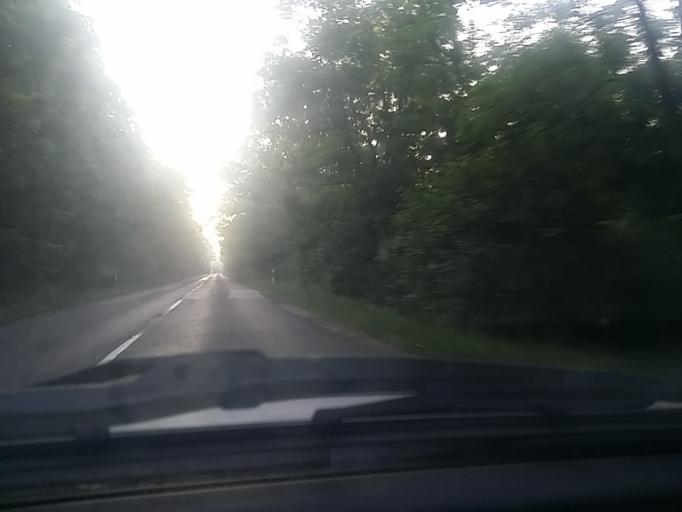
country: HU
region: Pest
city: Forropuszta
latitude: 47.4635
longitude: 19.6393
